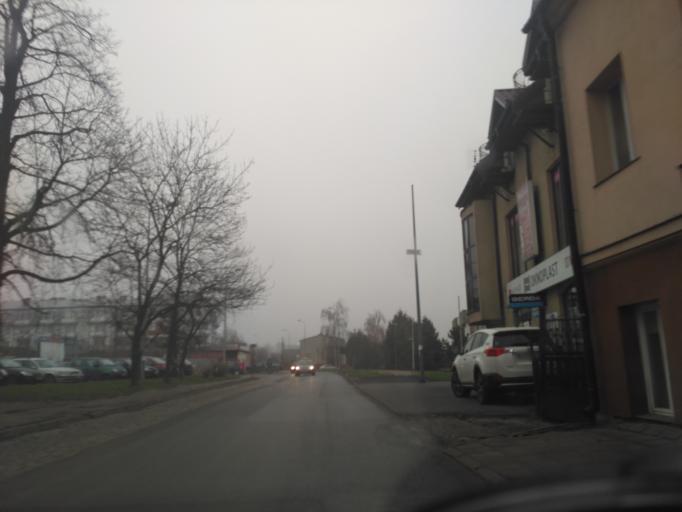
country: PL
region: Lublin Voivodeship
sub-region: Chelm
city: Chelm
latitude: 51.1297
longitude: 23.4722
